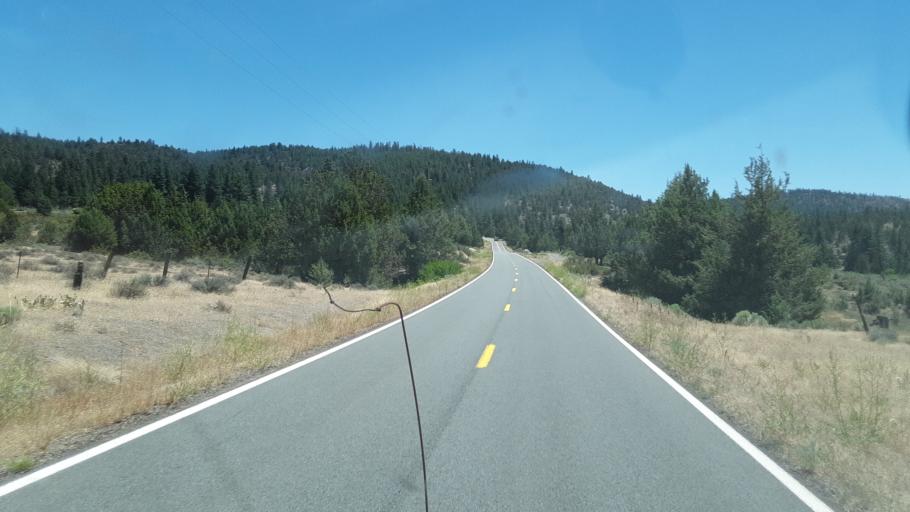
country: US
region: California
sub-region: Modoc County
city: Alturas
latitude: 41.0391
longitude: -120.8605
